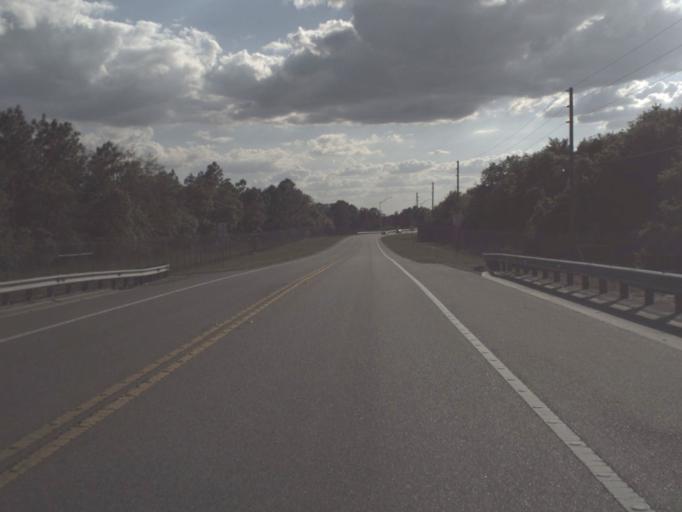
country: US
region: Florida
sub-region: Lake County
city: Mount Plymouth
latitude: 28.8145
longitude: -81.4987
